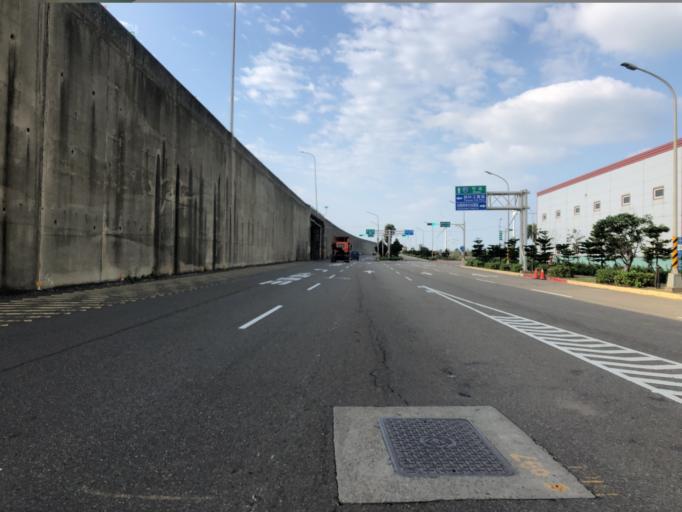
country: TW
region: Taiwan
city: Taoyuan City
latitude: 25.0519
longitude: 121.0888
